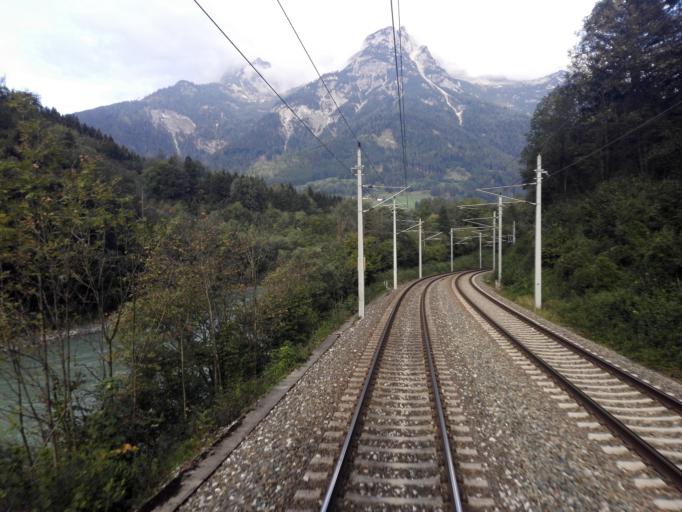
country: AT
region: Salzburg
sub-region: Politischer Bezirk Sankt Johann im Pongau
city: Werfen
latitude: 47.4899
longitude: 13.1807
